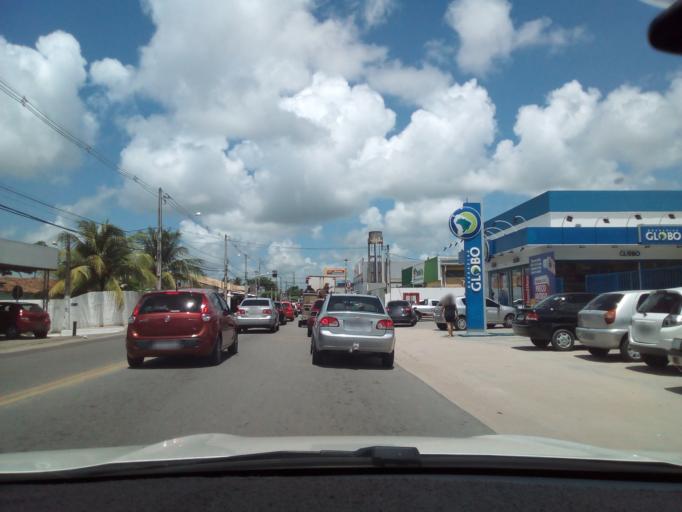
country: BR
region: Paraiba
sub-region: Joao Pessoa
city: Joao Pessoa
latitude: -7.1766
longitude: -34.8739
